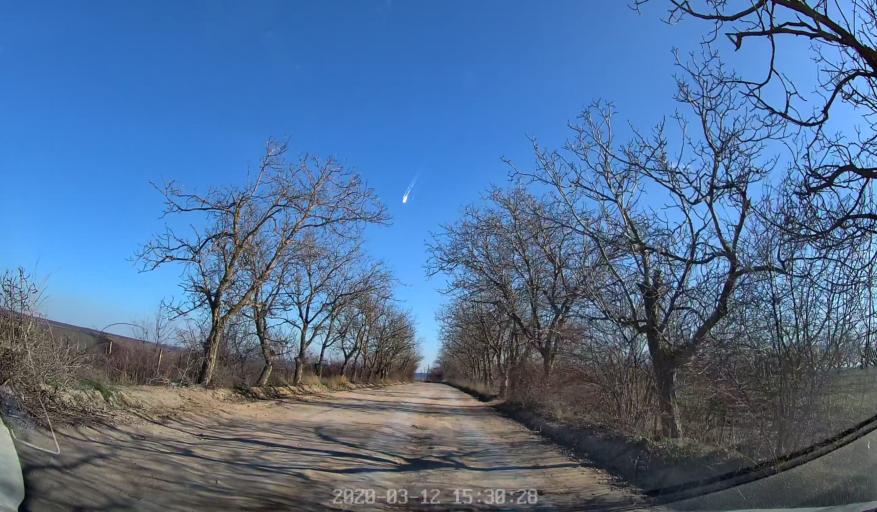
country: MD
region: Chisinau
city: Ciorescu
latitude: 47.1609
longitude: 28.9389
